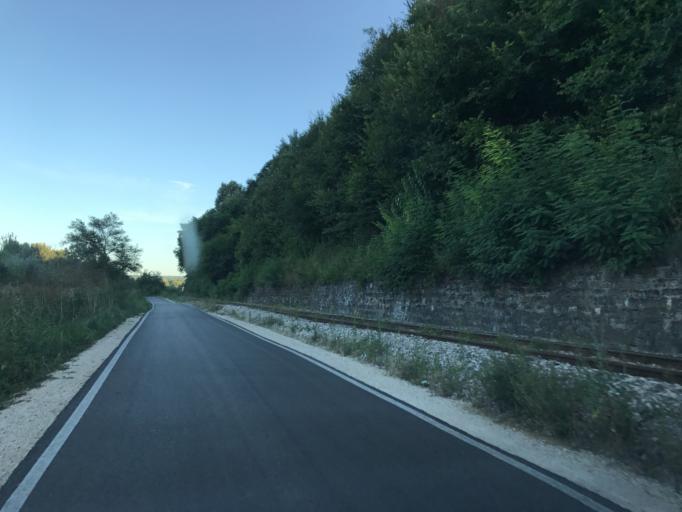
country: BG
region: Vidin
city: Bregovo
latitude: 44.1360
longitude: 22.6028
